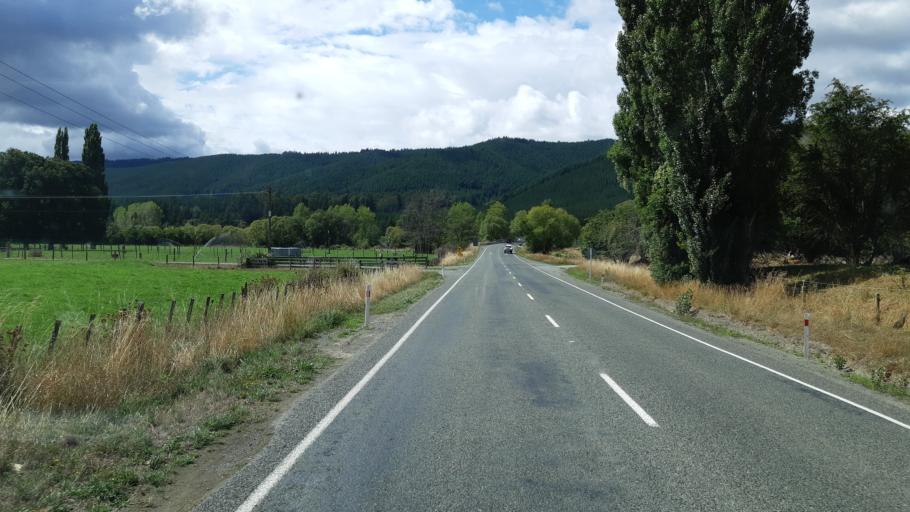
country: NZ
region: Tasman
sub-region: Tasman District
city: Wakefield
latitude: -41.4493
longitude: 172.8287
